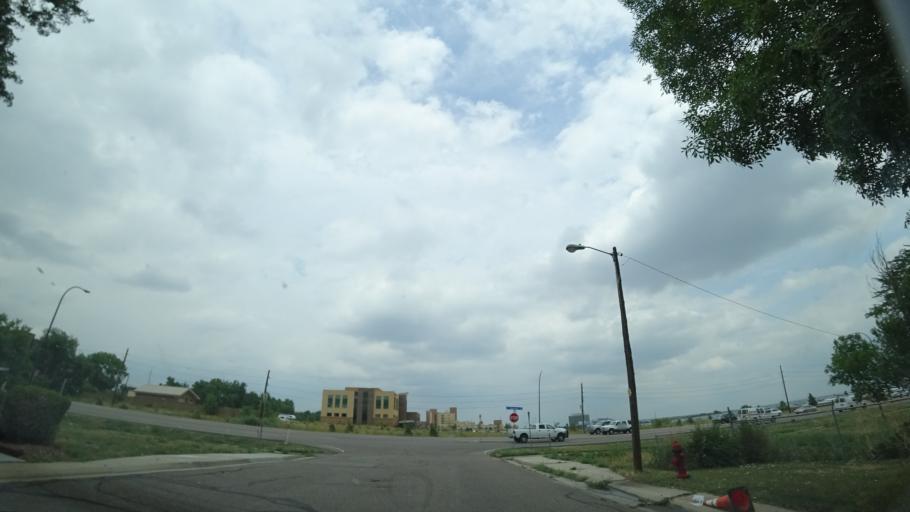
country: US
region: Colorado
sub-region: Jefferson County
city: Lakewood
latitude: 39.7101
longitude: -105.1293
